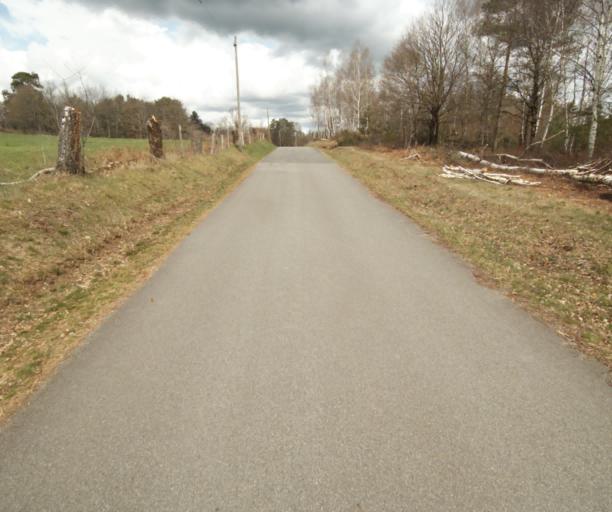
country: FR
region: Limousin
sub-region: Departement de la Correze
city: Correze
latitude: 45.3446
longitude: 1.9385
